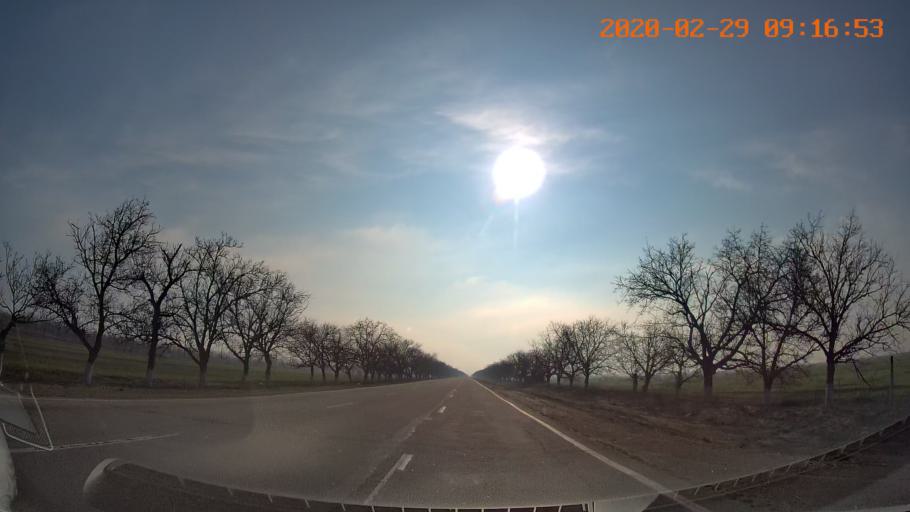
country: MD
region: Telenesti
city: Pervomaisc
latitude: 46.7879
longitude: 29.8943
